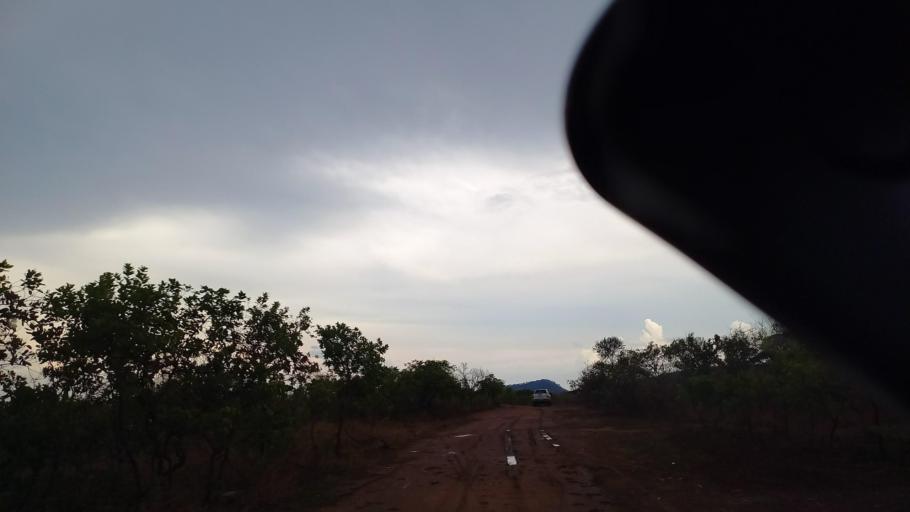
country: ZM
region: Lusaka
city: Kafue
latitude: -16.0257
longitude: 28.2984
